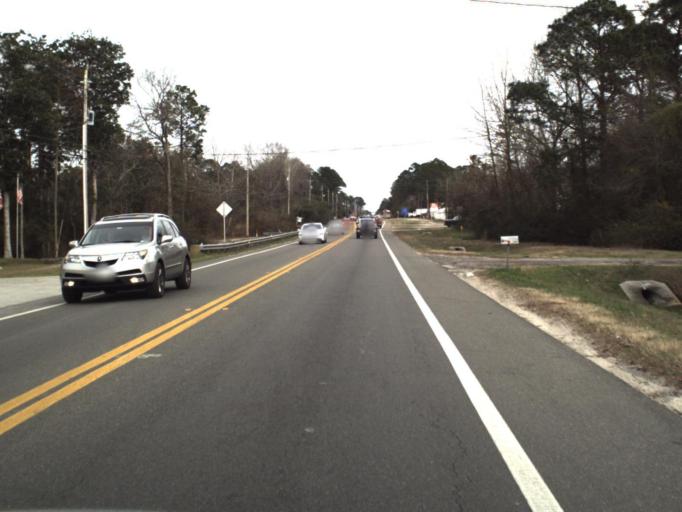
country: US
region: Florida
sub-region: Bay County
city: Callaway
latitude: 30.1530
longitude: -85.5863
